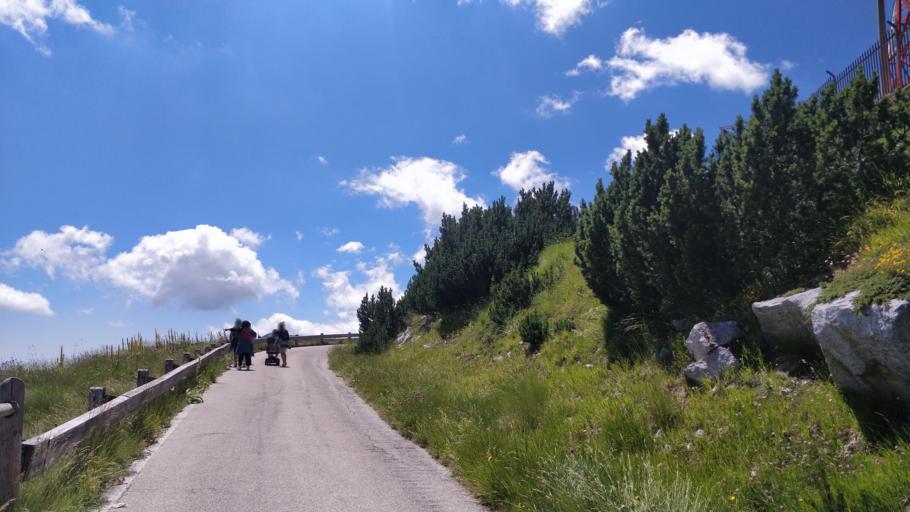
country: IT
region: Abruzzo
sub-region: Provincia di Chieti
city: Pretoro
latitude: 42.1589
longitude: 14.1331
